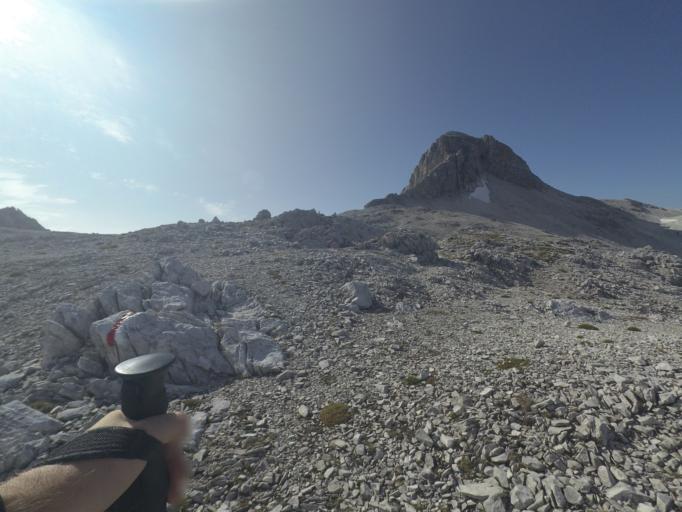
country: AT
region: Salzburg
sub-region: Politischer Bezirk Sankt Johann im Pongau
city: Kleinarl
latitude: 47.2098
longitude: 13.3995
